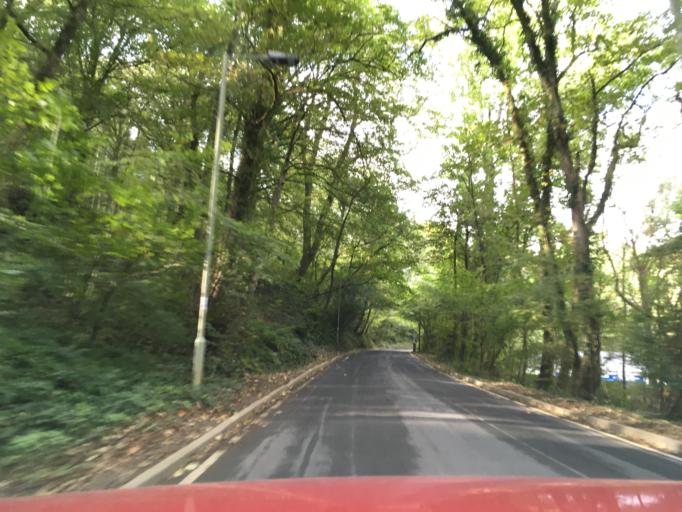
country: GB
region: Wales
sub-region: Cardiff
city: Pentyrch
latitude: 51.5412
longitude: -3.2737
